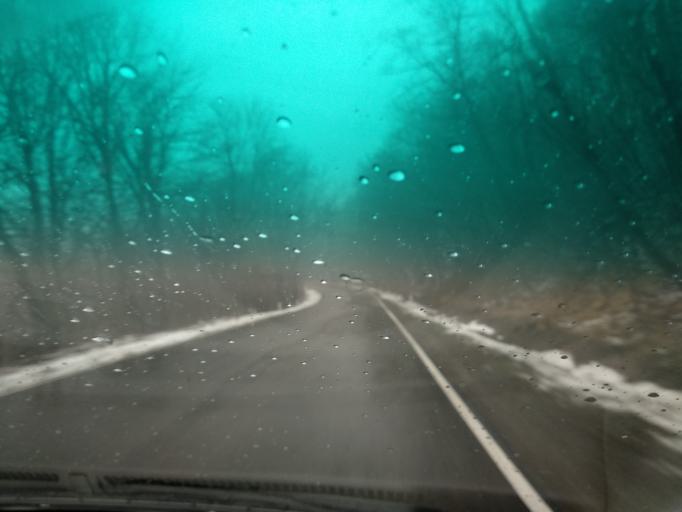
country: RU
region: Krasnodarskiy
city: Khadyzhensk
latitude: 44.2645
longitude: 39.3524
